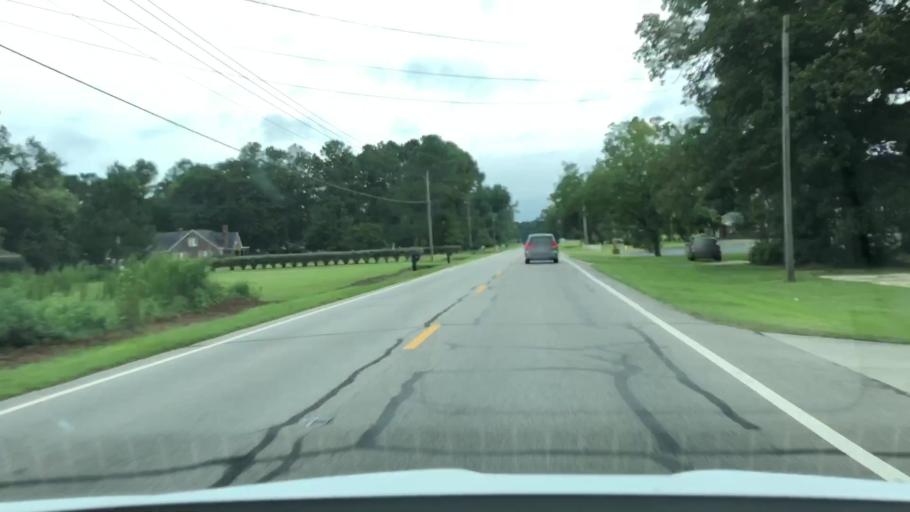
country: US
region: North Carolina
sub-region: Lenoir County
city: Kinston
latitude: 35.2122
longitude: -77.5688
